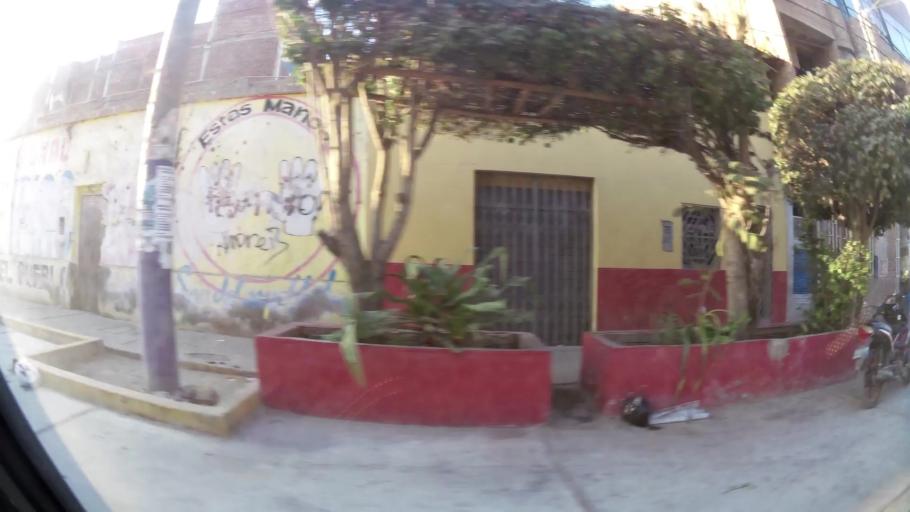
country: PE
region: Lambayeque
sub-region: Provincia de Chiclayo
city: Santa Rosa
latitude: -6.7697
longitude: -79.8315
